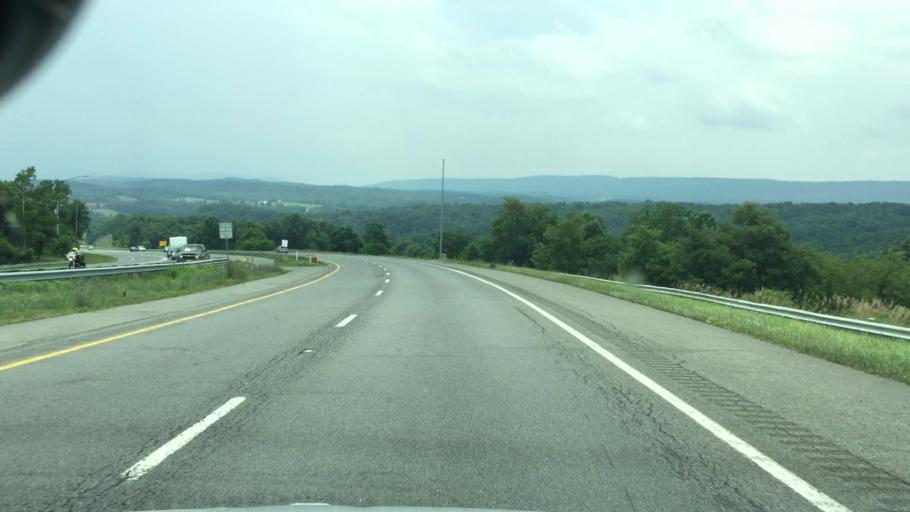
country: US
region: West Virginia
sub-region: Morgan County
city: Berkeley Springs
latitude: 39.7127
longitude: -78.3018
